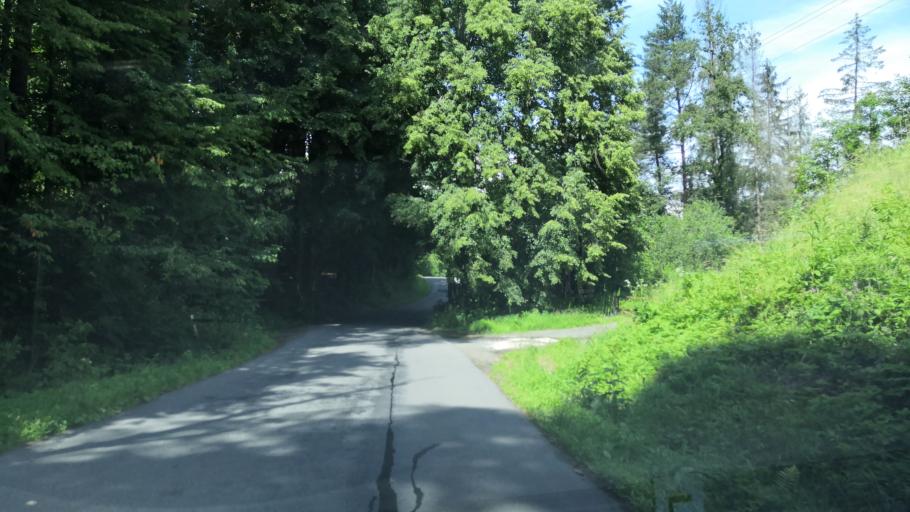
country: CZ
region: Zlin
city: Vidce
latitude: 49.4362
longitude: 18.0935
